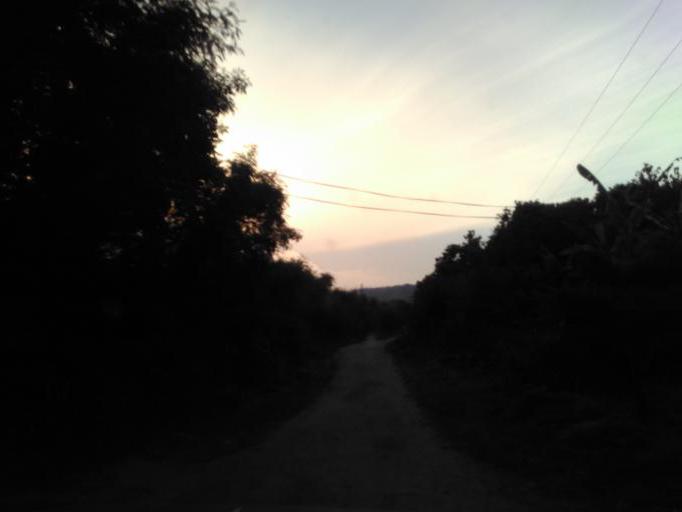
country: GH
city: Bekwai
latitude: 6.5173
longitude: -1.4407
